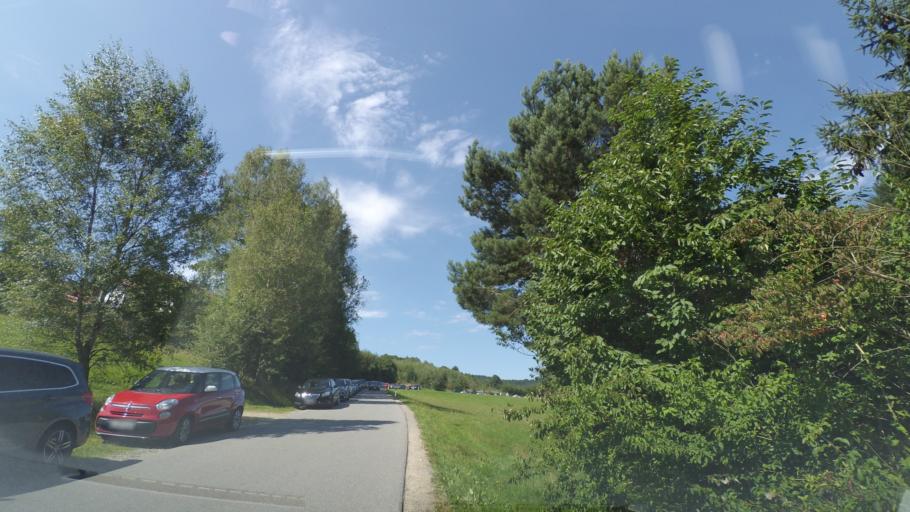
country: DE
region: Bavaria
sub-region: Upper Palatinate
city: Lohberg
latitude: 49.1720
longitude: 13.0861
